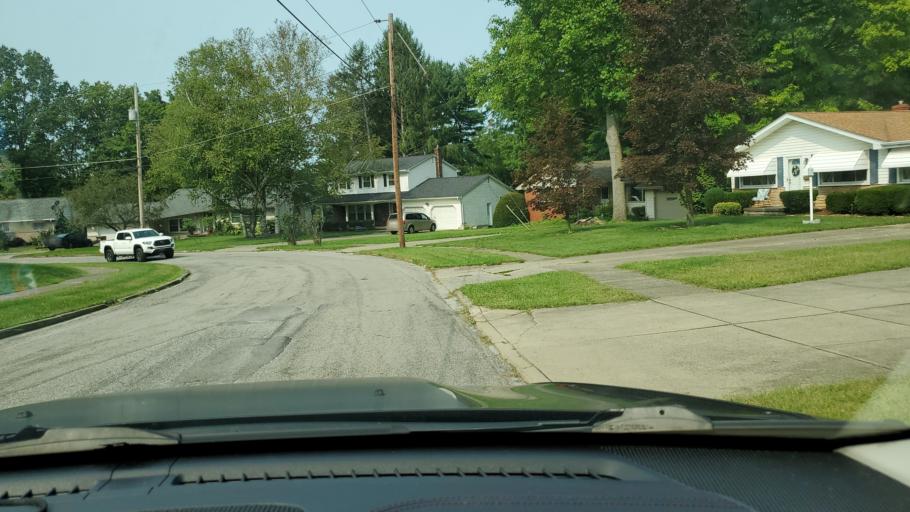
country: US
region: Ohio
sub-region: Mahoning County
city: Boardman
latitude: 41.0360
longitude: -80.6484
